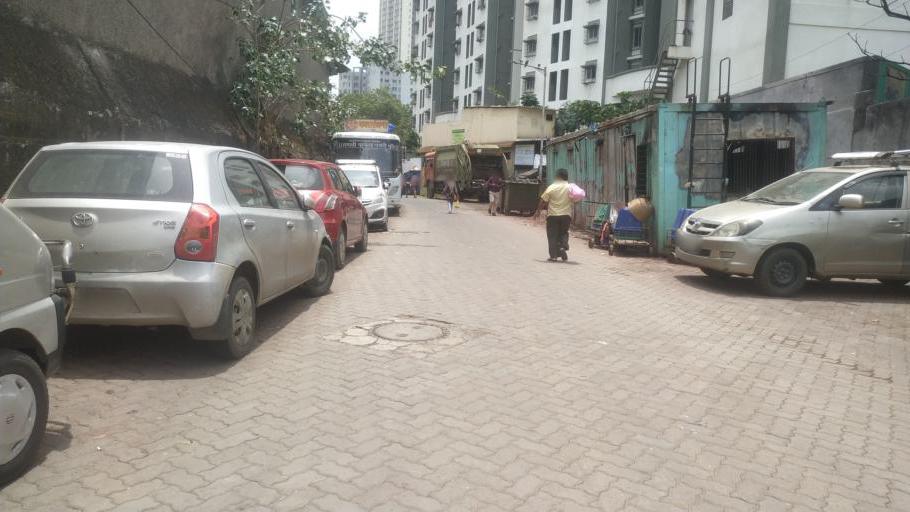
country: IN
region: Maharashtra
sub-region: Mumbai Suburban
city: Mumbai
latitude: 18.9893
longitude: 72.8379
